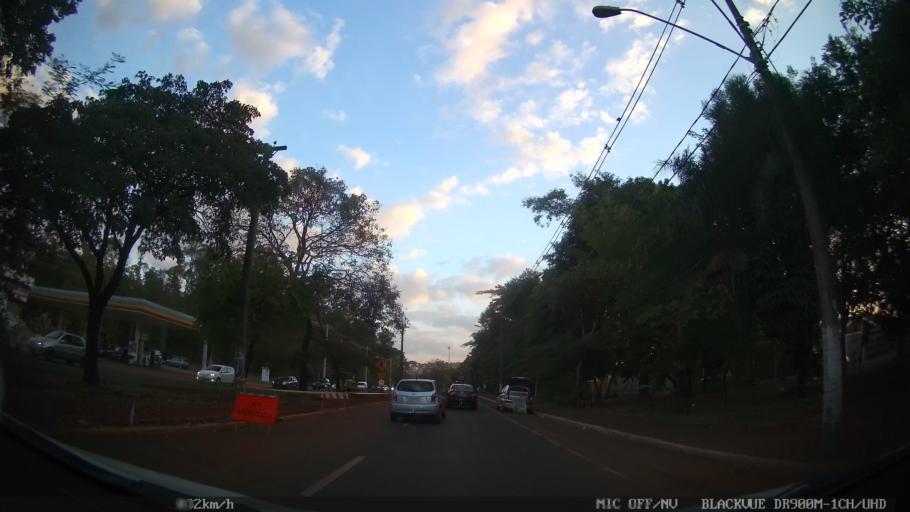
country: BR
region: Sao Paulo
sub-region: Ribeirao Preto
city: Ribeirao Preto
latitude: -21.1615
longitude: -47.7882
